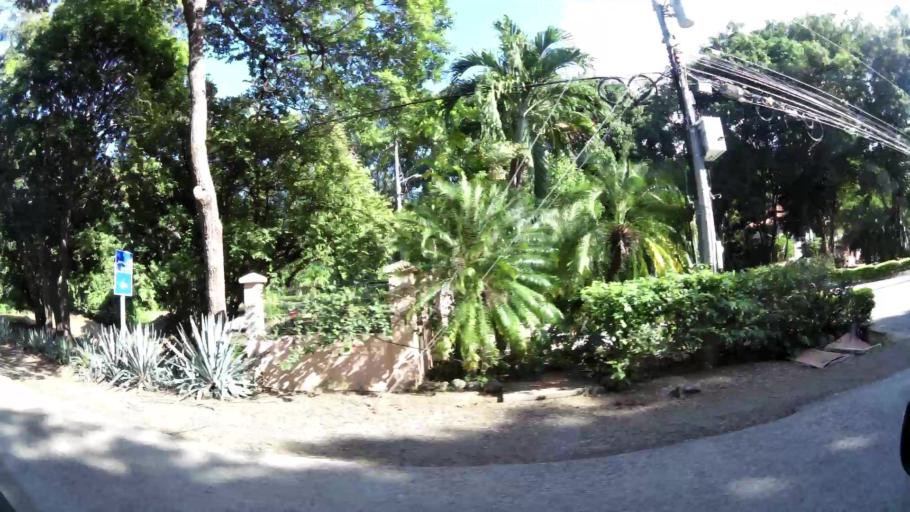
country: CR
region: Guanacaste
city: Sardinal
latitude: 10.5770
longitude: -85.6720
